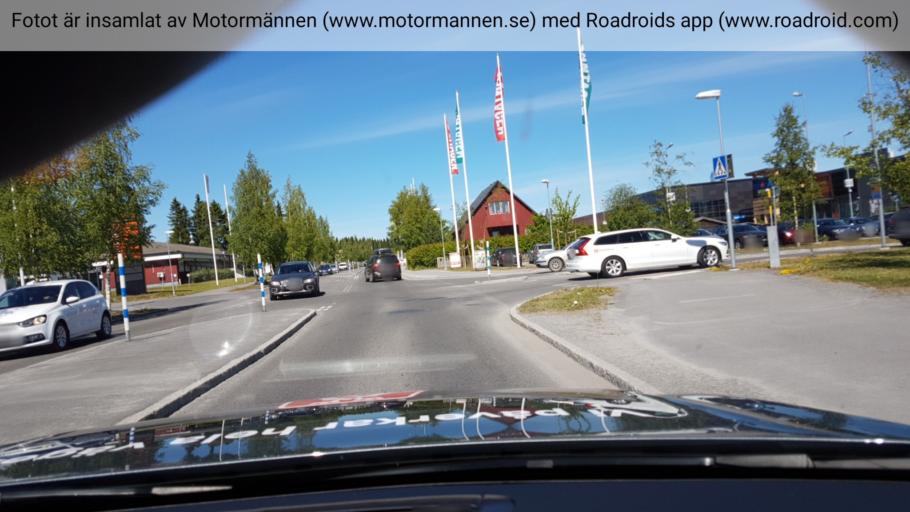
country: SE
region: Jaemtland
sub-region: OEstersunds Kommun
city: Ostersund
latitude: 63.1711
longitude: 14.6900
